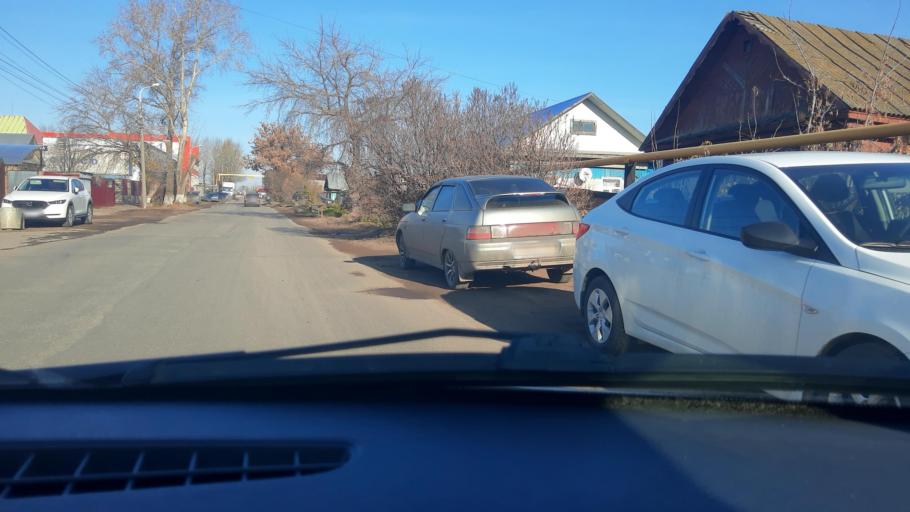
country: RU
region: Bashkortostan
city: Mikhaylovka
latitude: 54.6949
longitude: 55.8493
